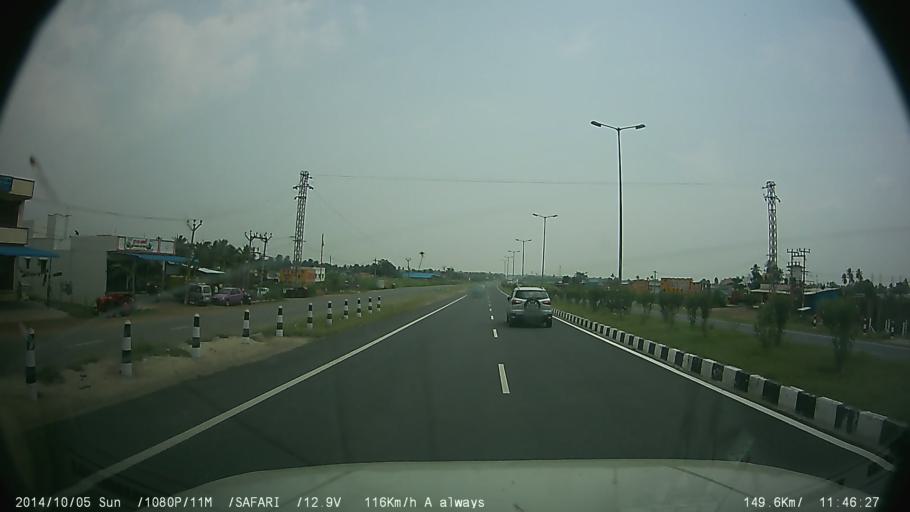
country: IN
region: Tamil Nadu
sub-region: Salem
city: Attur
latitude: 11.5910
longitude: 78.6677
